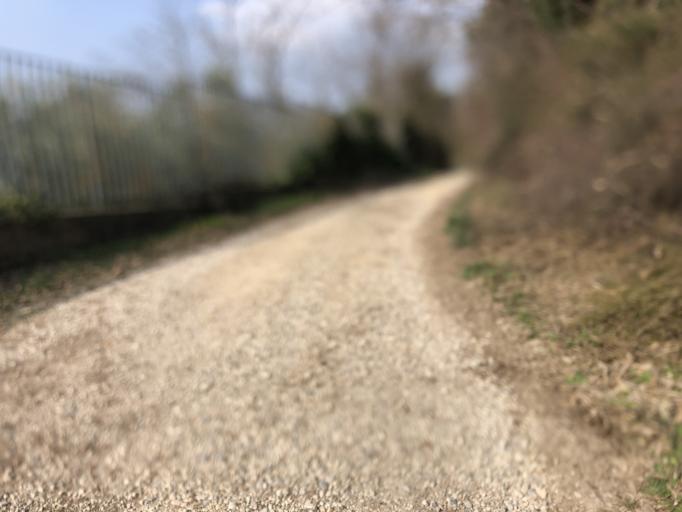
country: IT
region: Veneto
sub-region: Provincia di Verona
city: Sona
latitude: 45.4275
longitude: 10.8382
